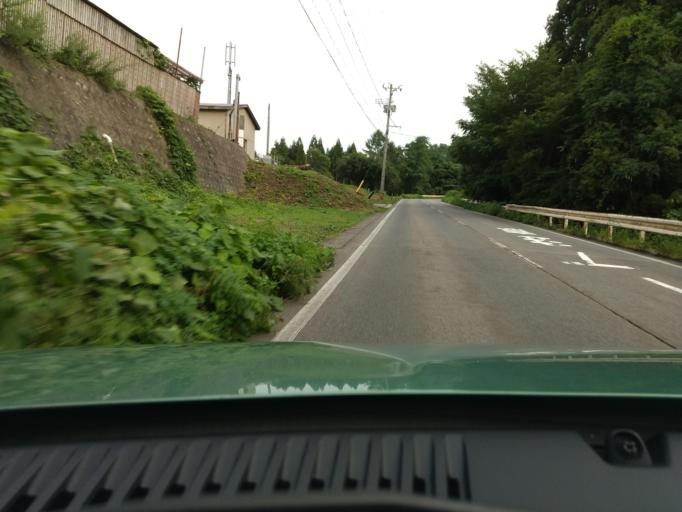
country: JP
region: Akita
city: Akita
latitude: 39.7779
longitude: 140.1341
